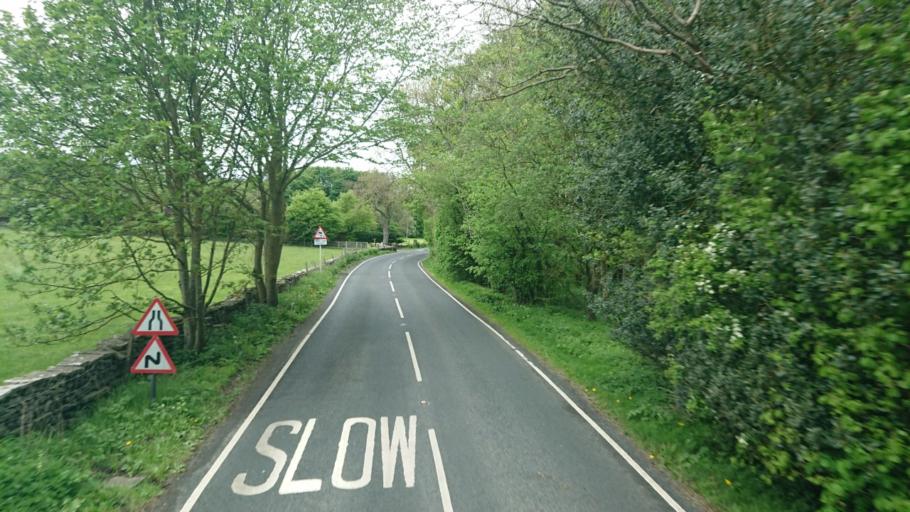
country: GB
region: England
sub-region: North Yorkshire
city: Leyburn
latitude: 54.2946
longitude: -1.9637
